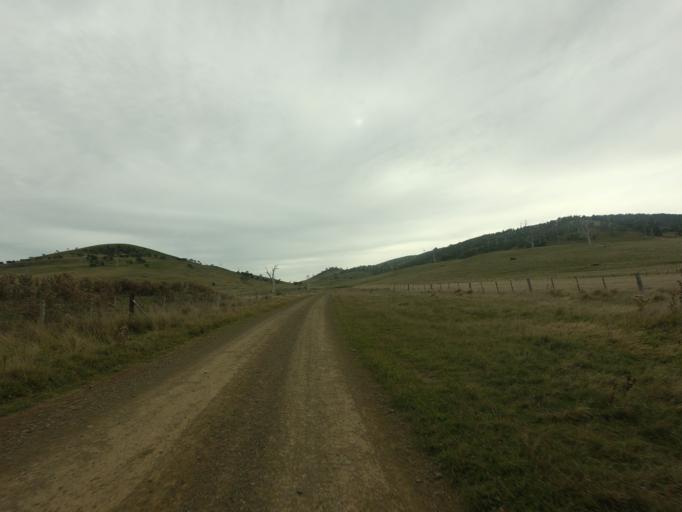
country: AU
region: Tasmania
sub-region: Derwent Valley
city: New Norfolk
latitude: -42.3815
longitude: 146.8683
